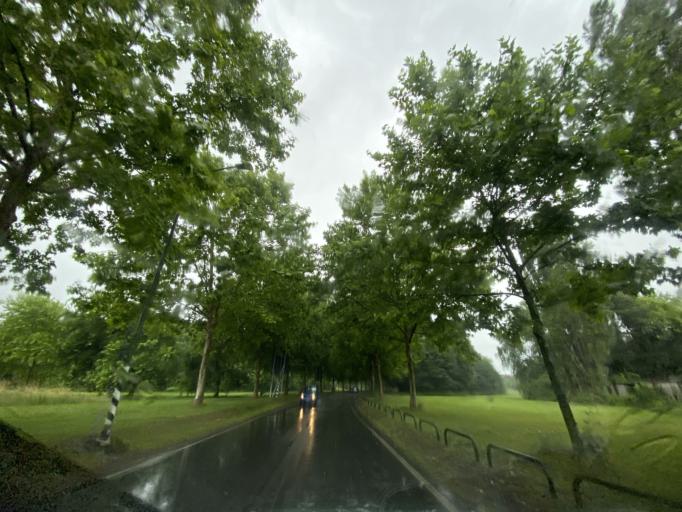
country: IT
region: Lombardy
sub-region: Citta metropolitana di Milano
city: Bresso
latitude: 45.5309
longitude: 9.1787
